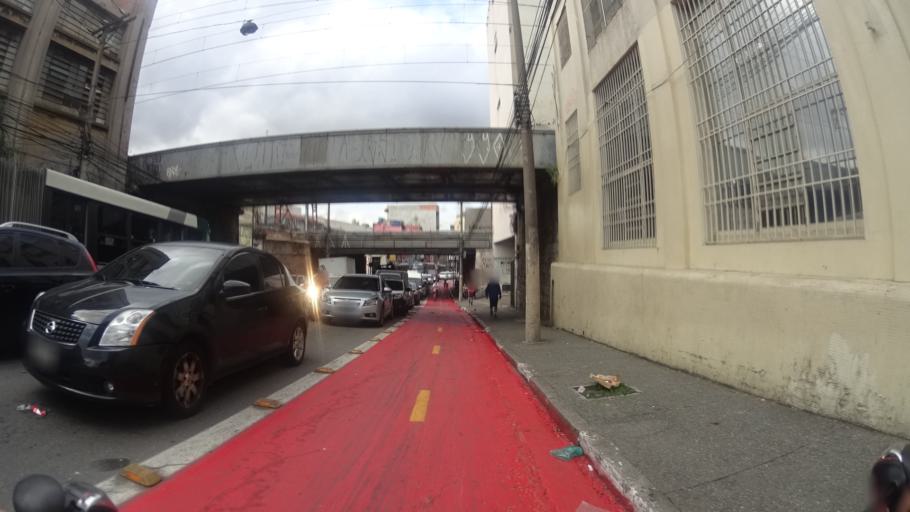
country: BR
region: Sao Paulo
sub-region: Sao Paulo
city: Sao Paulo
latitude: -23.5305
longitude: -46.6426
